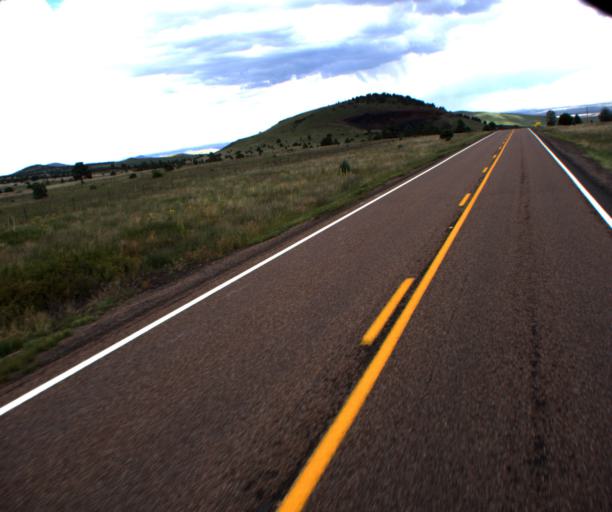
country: US
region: Arizona
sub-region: Apache County
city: Eagar
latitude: 34.0864
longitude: -109.4425
